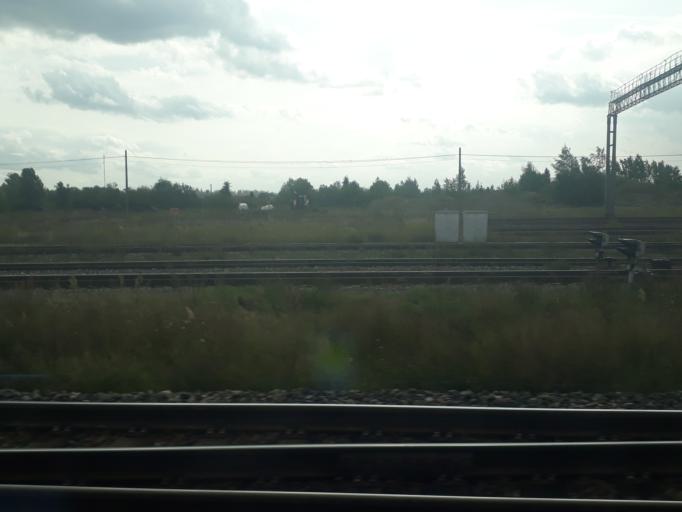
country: EE
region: Laeaene-Virumaa
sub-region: Tapa vald
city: Tapa
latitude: 59.2632
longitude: 25.9302
